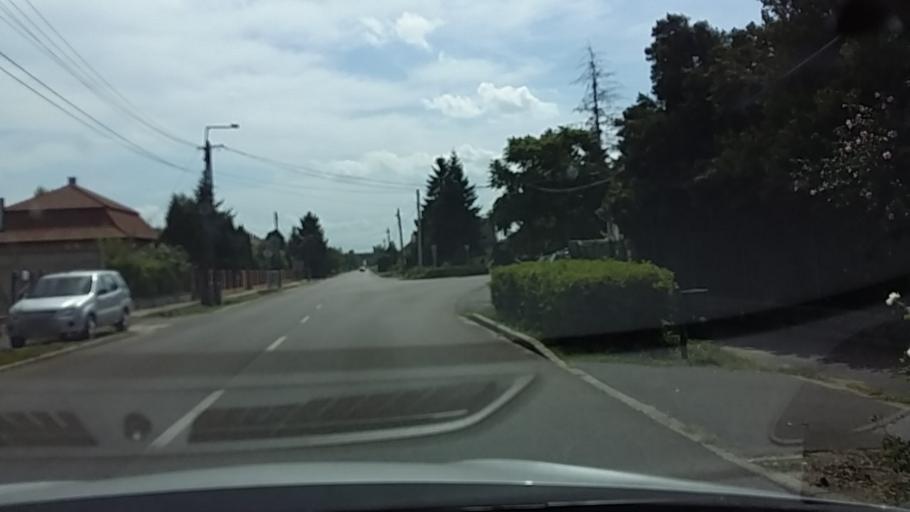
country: HU
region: Borsod-Abauj-Zemplen
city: Nyekladhaza
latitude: 47.9911
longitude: 20.8366
